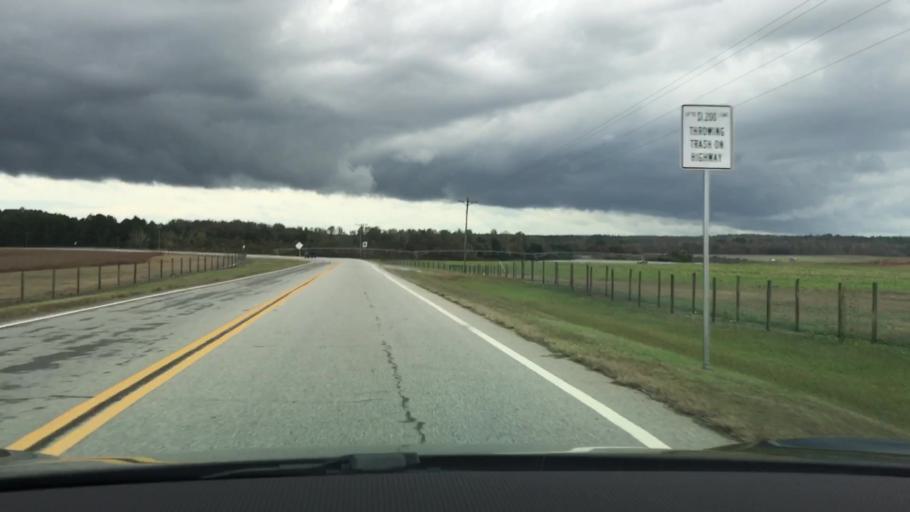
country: US
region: Georgia
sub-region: Oconee County
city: Watkinsville
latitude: 33.7266
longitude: -83.3023
